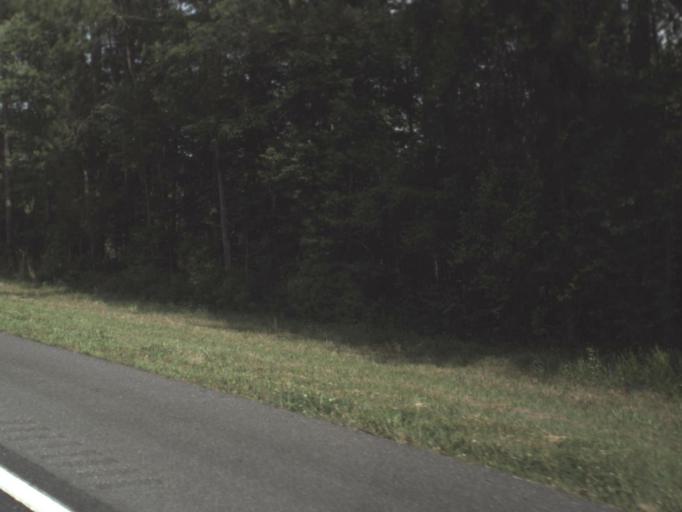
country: US
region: Florida
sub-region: Baker County
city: Macclenny
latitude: 30.2501
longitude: -82.2169
